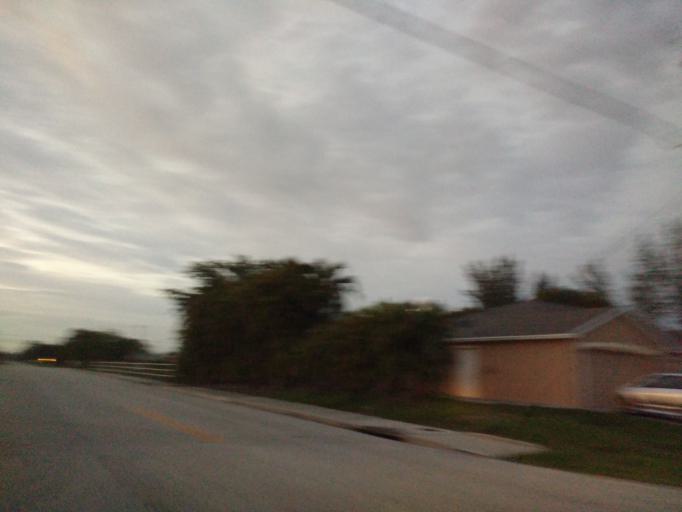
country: US
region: Florida
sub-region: Lee County
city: Cape Coral
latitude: 26.6139
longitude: -81.9733
